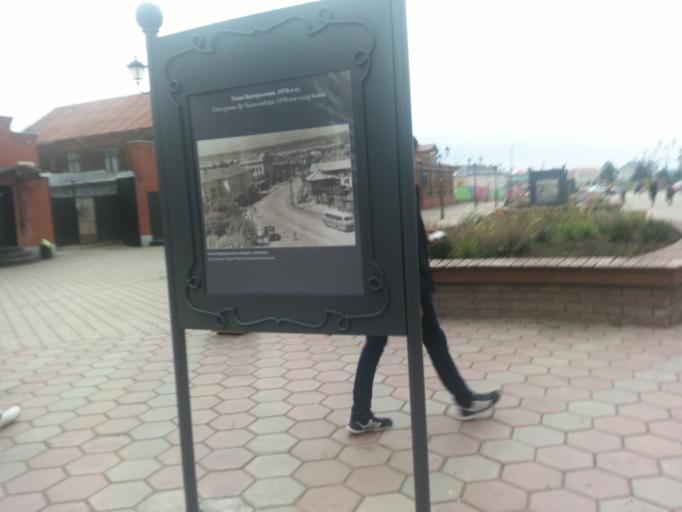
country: RU
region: Tatarstan
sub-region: Tukayevskiy Rayon
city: Naberezhnyye Chelny
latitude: 55.6999
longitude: 52.3160
